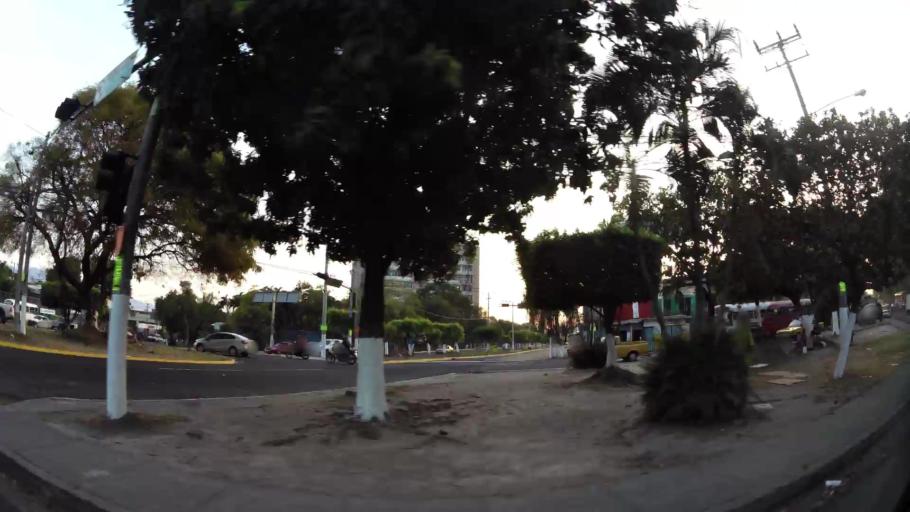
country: SV
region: San Salvador
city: Mejicanos
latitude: 13.7155
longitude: -89.2037
